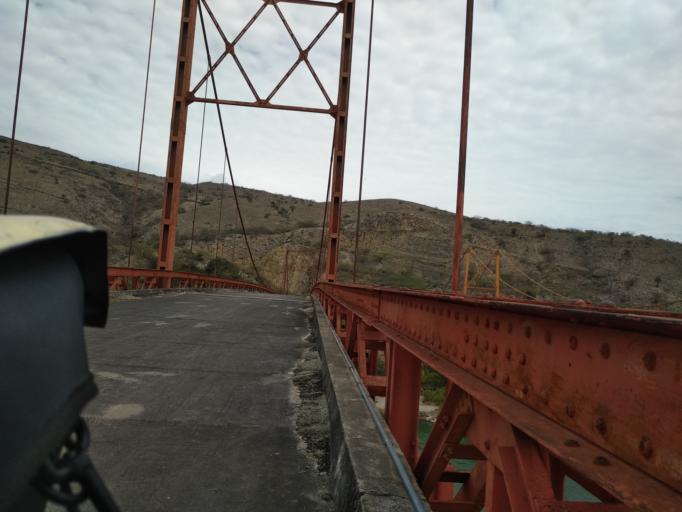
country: PE
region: Cajamarca
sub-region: Provincia de Jaen
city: Bellavista
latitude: -5.7546
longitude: -78.6924
